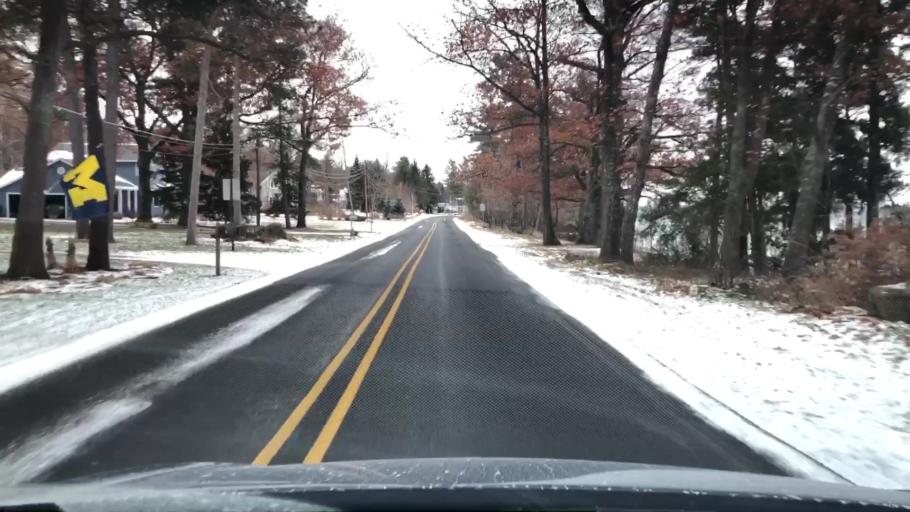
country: US
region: Michigan
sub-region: Grand Traverse County
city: Traverse City
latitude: 44.8145
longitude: -85.5782
